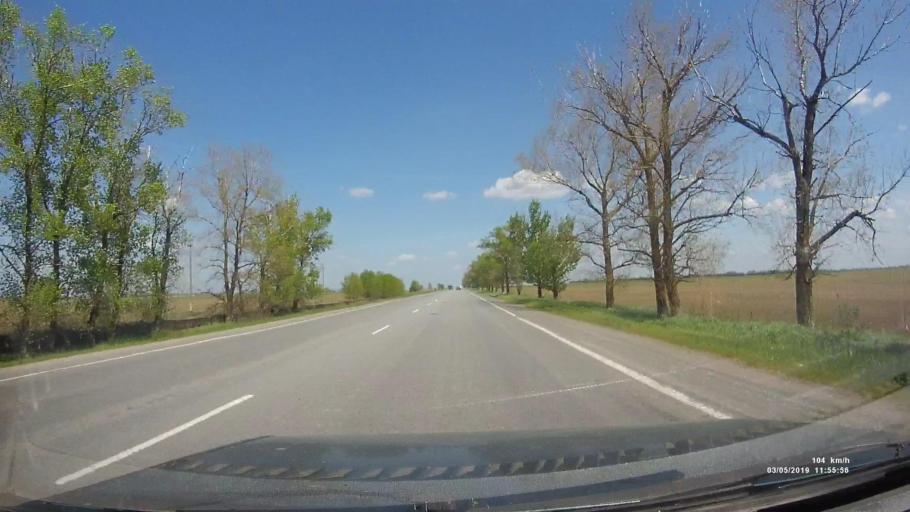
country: RU
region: Rostov
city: Bagayevskaya
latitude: 47.1876
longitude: 40.2959
